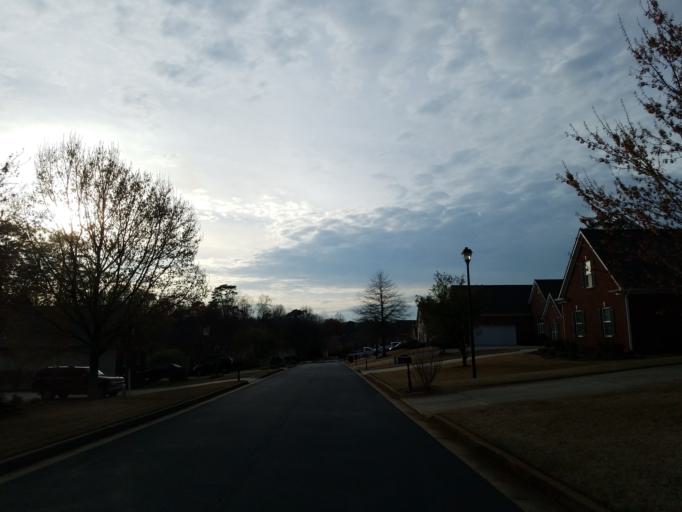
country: US
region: Georgia
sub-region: Dawson County
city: Dawsonville
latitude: 34.4273
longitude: -84.1227
